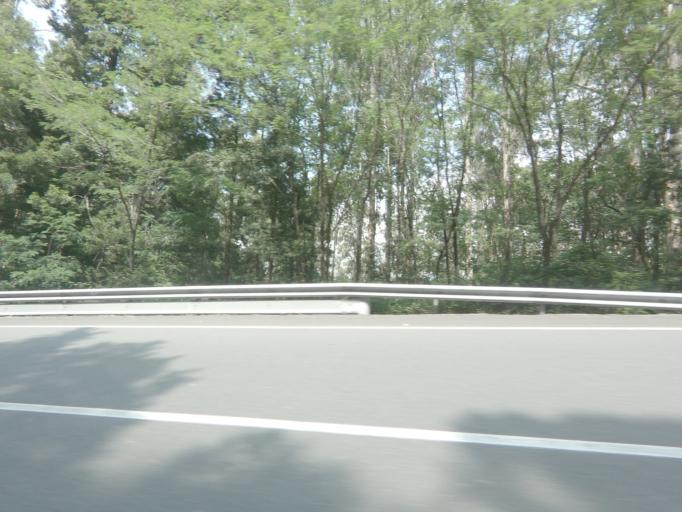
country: ES
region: Galicia
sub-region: Provincia de Pontevedra
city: Gondomar
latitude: 42.0948
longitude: -8.7567
